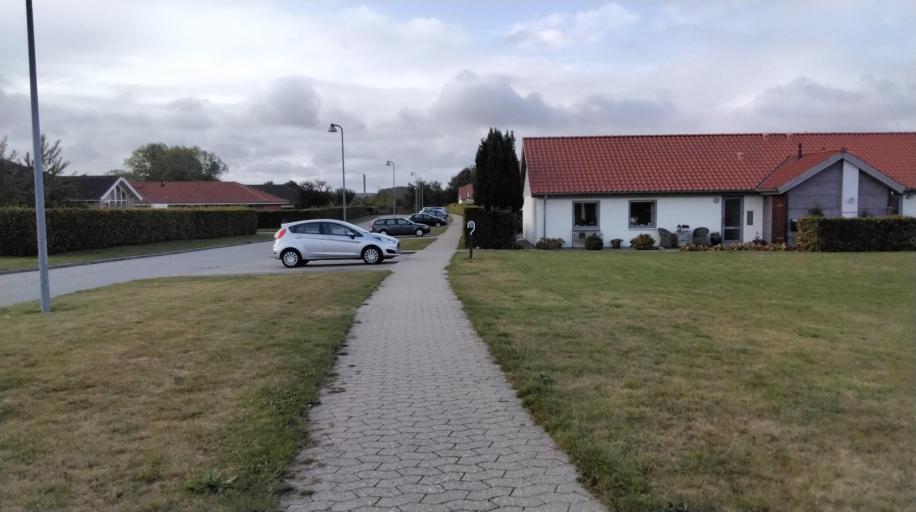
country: DK
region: Zealand
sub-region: Naestved Kommune
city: Naestved
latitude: 55.2242
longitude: 11.7280
